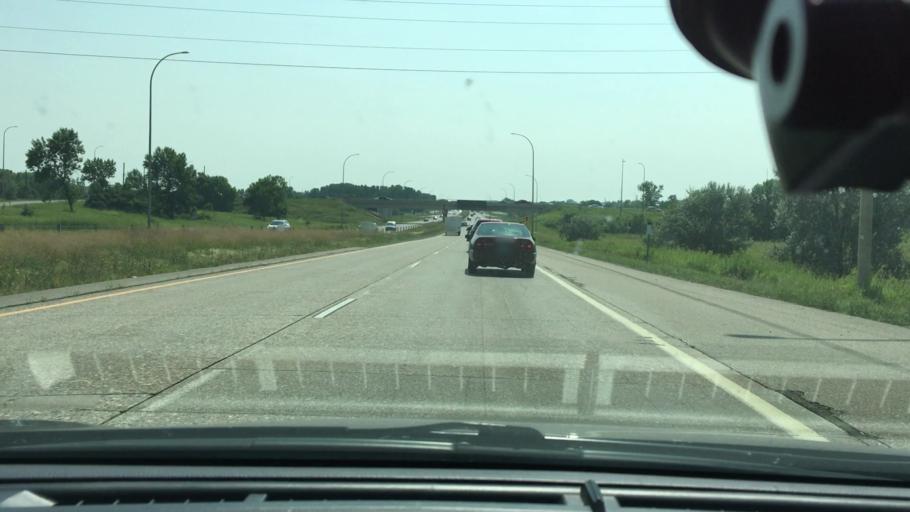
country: US
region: Minnesota
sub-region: Hennepin County
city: Osseo
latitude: 45.0971
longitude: -93.4026
